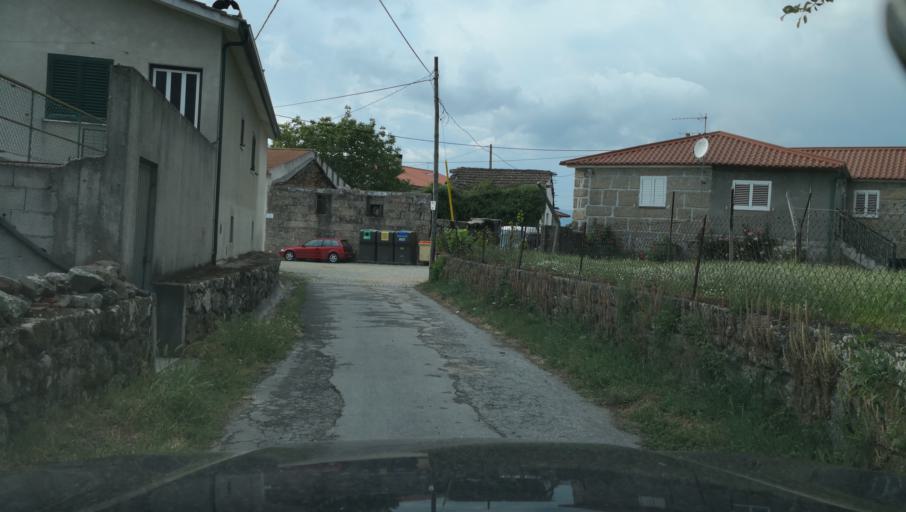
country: PT
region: Vila Real
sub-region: Vila Real
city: Vila Real
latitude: 41.3098
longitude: -7.6975
